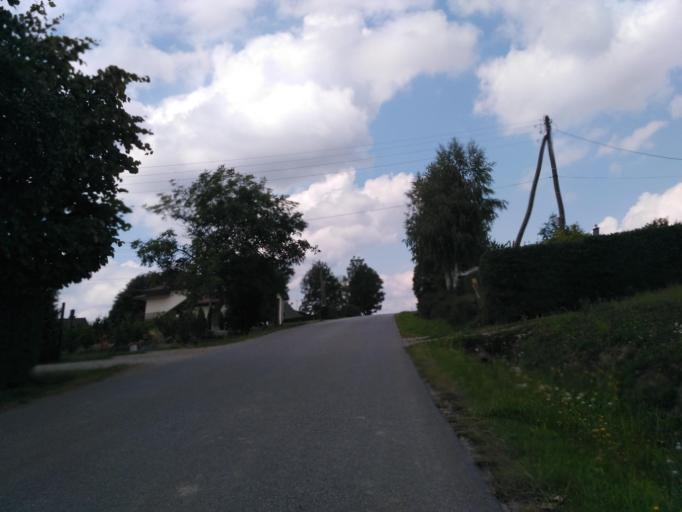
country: PL
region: Subcarpathian Voivodeship
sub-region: Powiat krosnienski
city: Iwonicz-Zdroj
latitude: 49.5847
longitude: 21.7422
